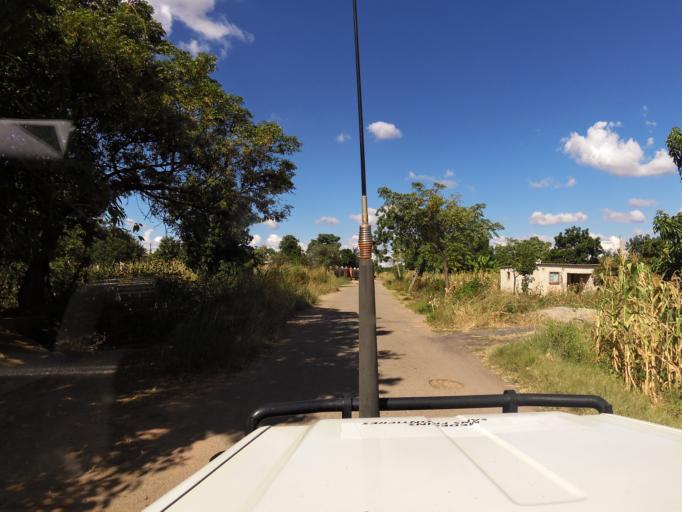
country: ZW
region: Harare
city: Epworth
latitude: -17.8712
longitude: 31.1412
